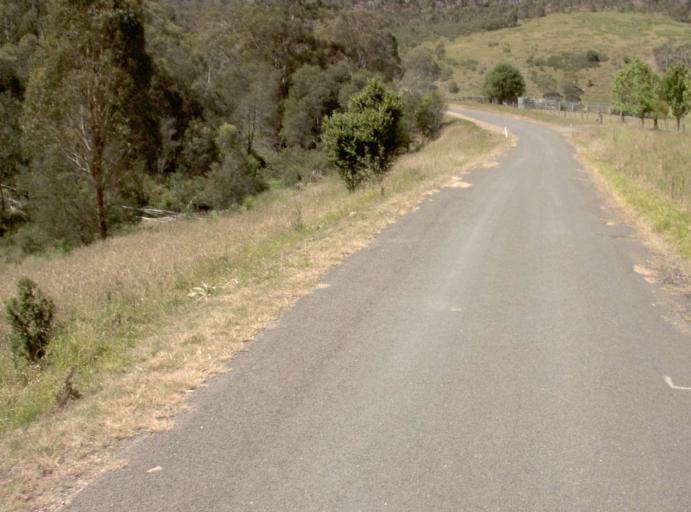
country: AU
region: New South Wales
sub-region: Bombala
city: Bombala
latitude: -37.1340
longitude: 148.6634
